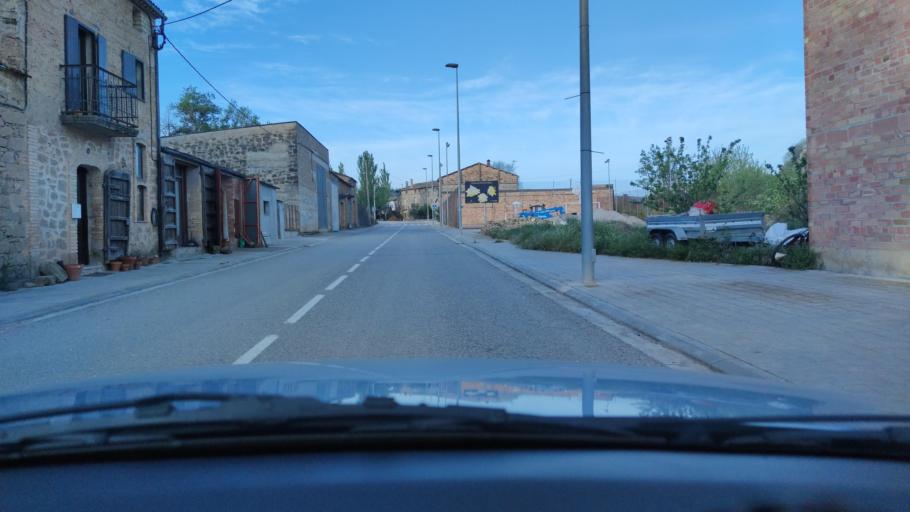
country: ES
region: Catalonia
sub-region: Provincia de Lleida
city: Ponts
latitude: 41.8761
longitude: 1.1768
